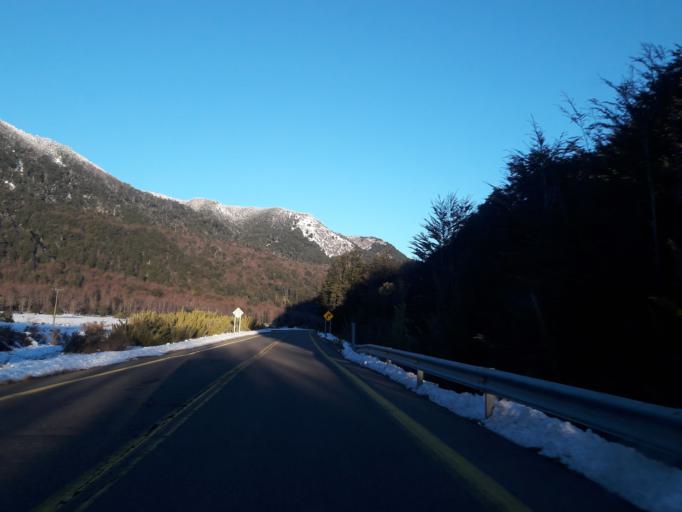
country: CL
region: Araucania
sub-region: Provincia de Cautin
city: Vilcun
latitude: -38.4886
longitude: -71.5275
